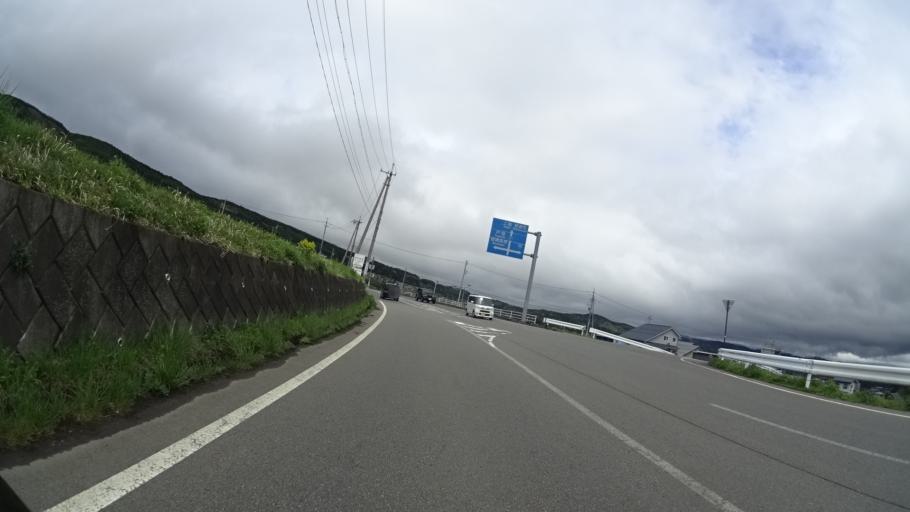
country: JP
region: Nagano
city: Nagano-shi
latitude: 36.7320
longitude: 138.2085
